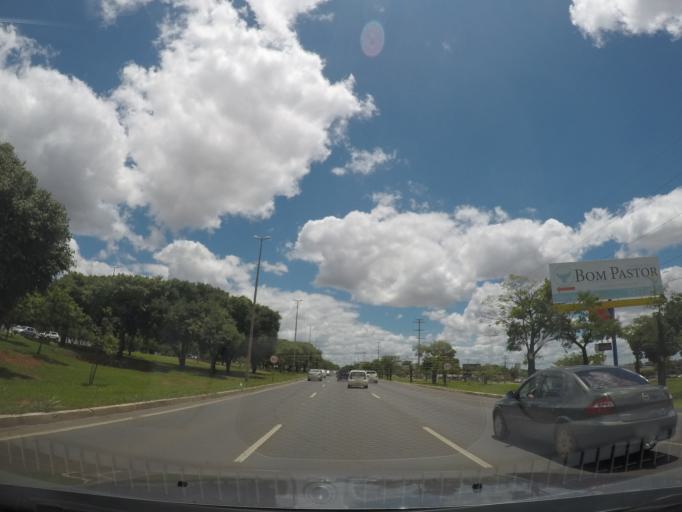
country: BR
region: Federal District
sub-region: Brasilia
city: Brasilia
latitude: -15.7903
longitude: -47.9431
